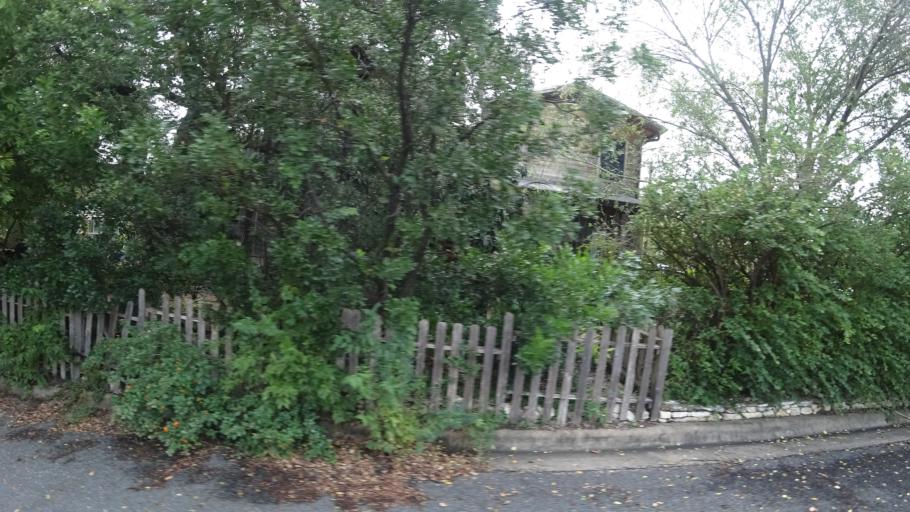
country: US
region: Texas
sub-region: Travis County
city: Austin
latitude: 30.2515
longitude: -97.7621
